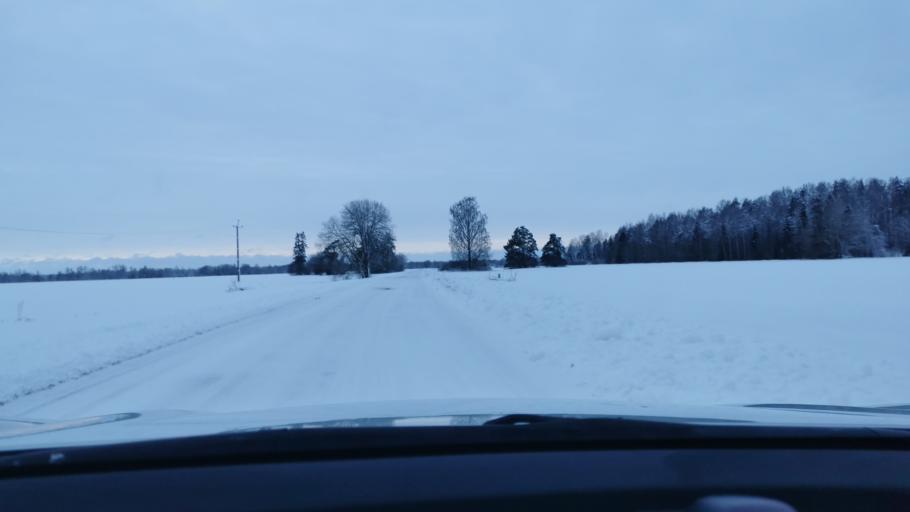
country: EE
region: Laeaene-Virumaa
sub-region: Viru-Nigula vald
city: Kunda
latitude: 59.4606
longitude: 26.5400
